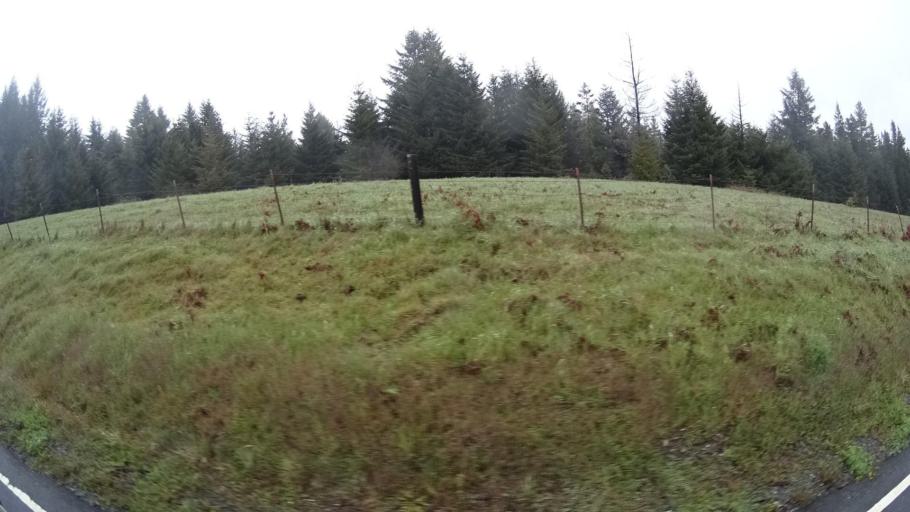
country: US
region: California
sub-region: Humboldt County
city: Westhaven-Moonstone
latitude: 41.1768
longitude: -123.9216
